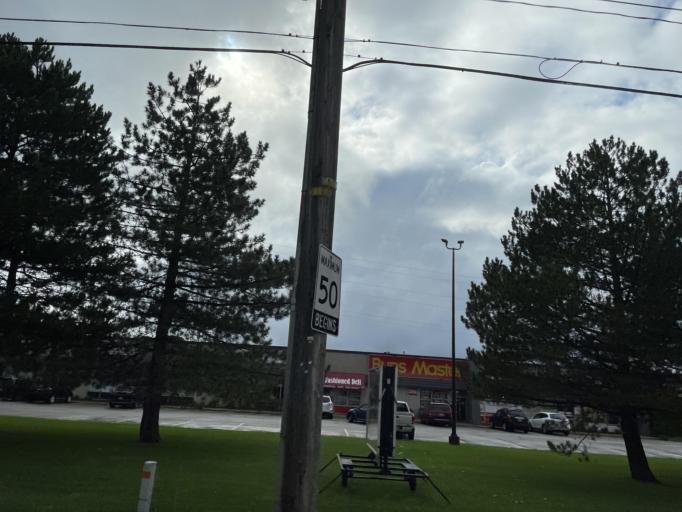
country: CA
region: Ontario
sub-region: Wellington County
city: Guelph
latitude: 43.5457
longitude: -80.2884
